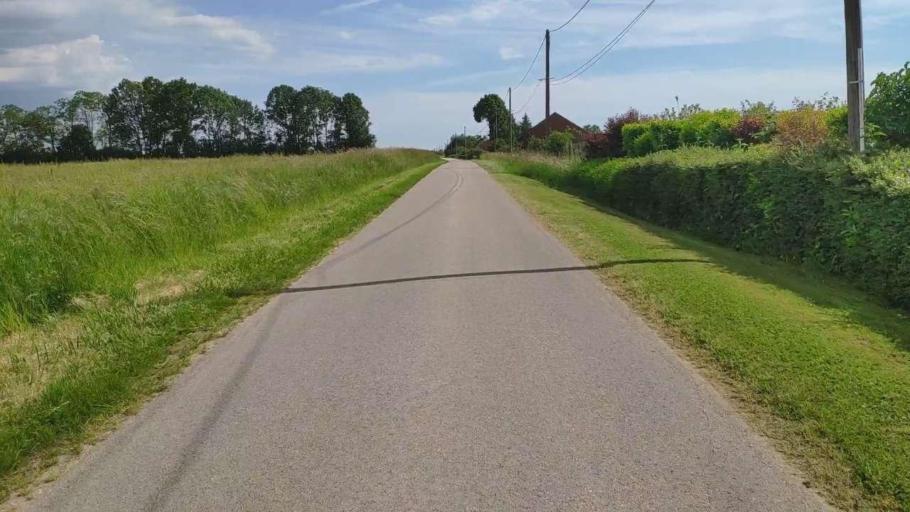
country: FR
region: Franche-Comte
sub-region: Departement du Jura
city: Bletterans
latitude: 46.8193
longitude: 5.3797
